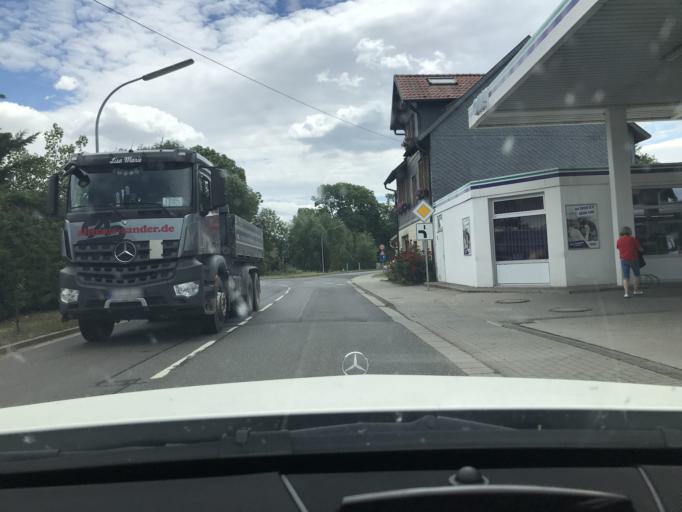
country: DE
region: Thuringia
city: Ebeleben
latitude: 51.2858
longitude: 10.7295
